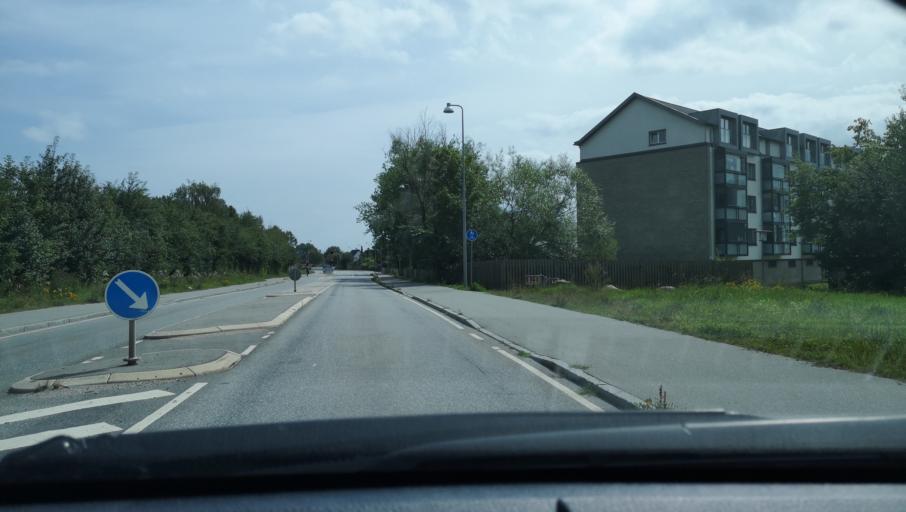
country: DK
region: Zealand
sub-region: Solrod Kommune
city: Solrod
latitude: 55.5015
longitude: 12.1873
